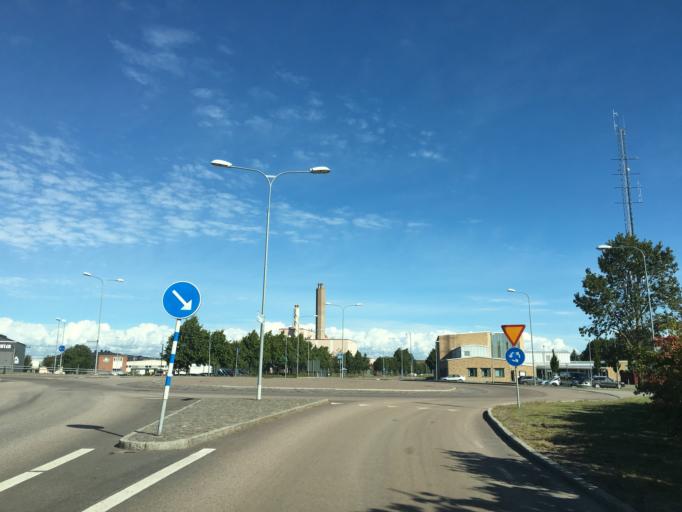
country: SE
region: Kalmar
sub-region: Kalmar Kommun
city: Kalmar
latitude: 56.6655
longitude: 16.3434
